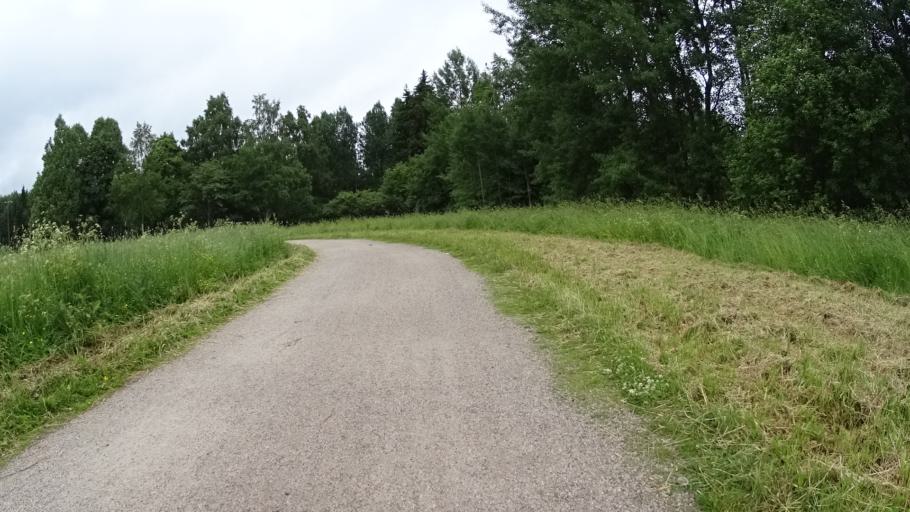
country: FI
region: Uusimaa
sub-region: Helsinki
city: Teekkarikylae
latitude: 60.2757
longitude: 24.8826
